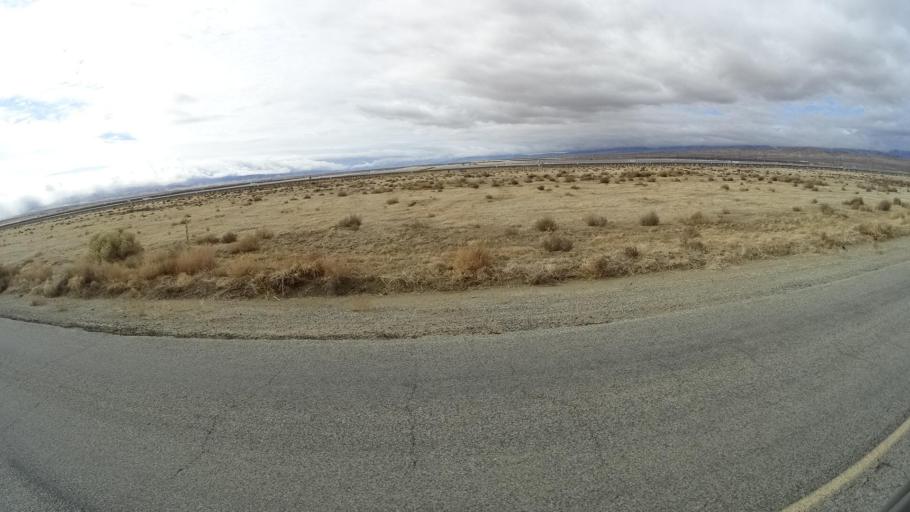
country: US
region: California
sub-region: Los Angeles County
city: Green Valley
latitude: 34.8292
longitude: -118.4317
